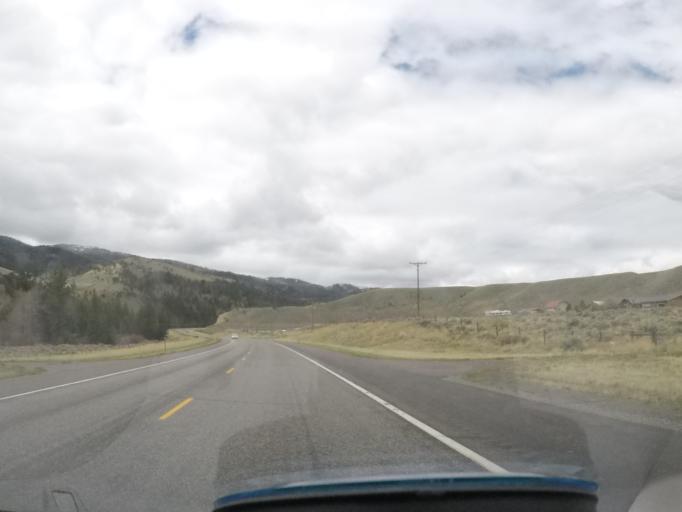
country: US
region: Wyoming
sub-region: Sublette County
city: Pinedale
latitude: 43.5793
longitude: -109.7476
